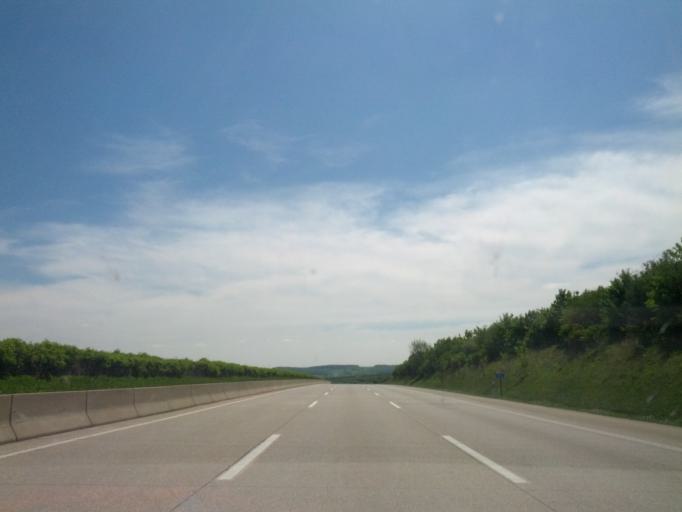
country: DE
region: Thuringia
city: Mellingen
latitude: 50.9146
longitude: 11.4120
